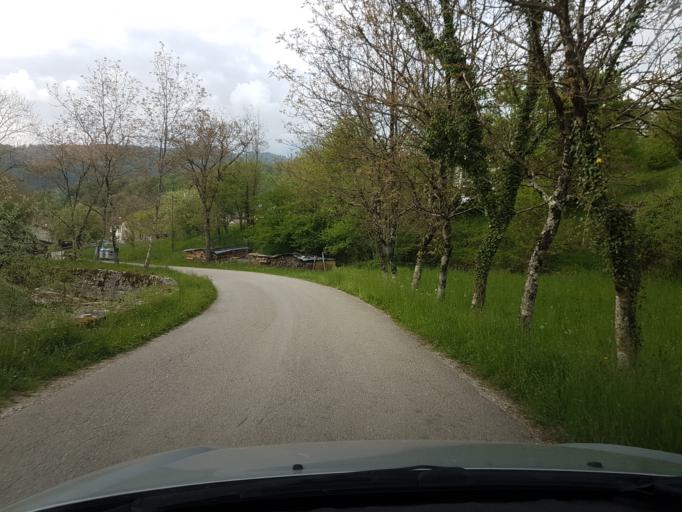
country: IT
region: Friuli Venezia Giulia
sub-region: Provincia di Udine
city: San Leonardo
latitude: 46.1171
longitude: 13.5322
